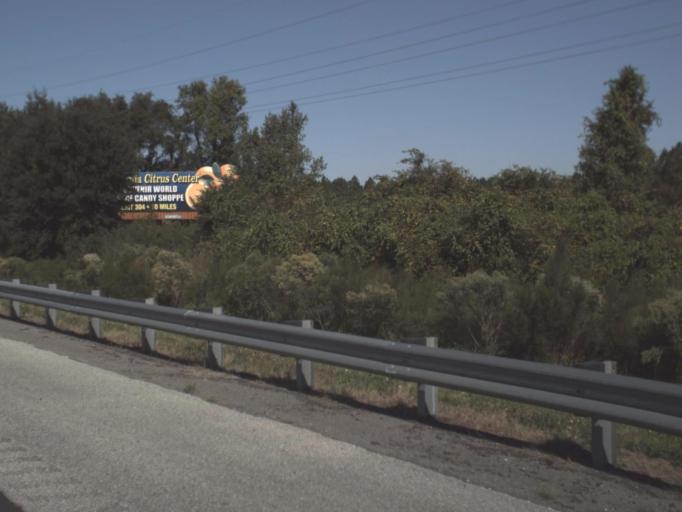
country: US
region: Florida
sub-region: Lake County
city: Hawthorne
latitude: 28.7587
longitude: -81.9421
